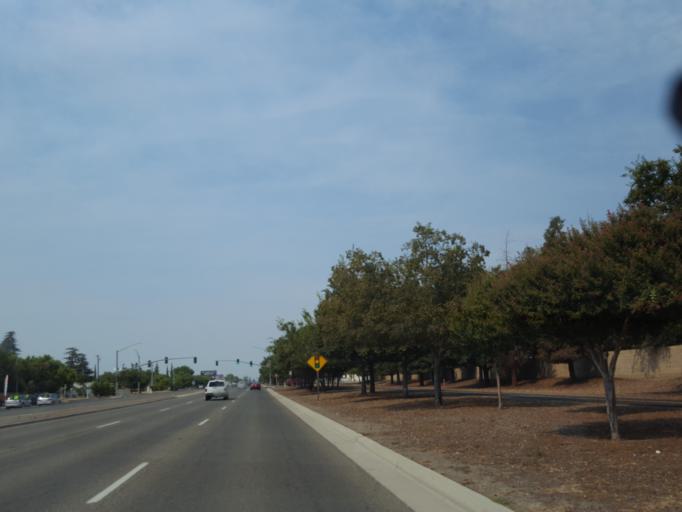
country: US
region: California
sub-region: Fresno County
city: Tarpey Village
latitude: 36.7851
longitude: -119.7003
